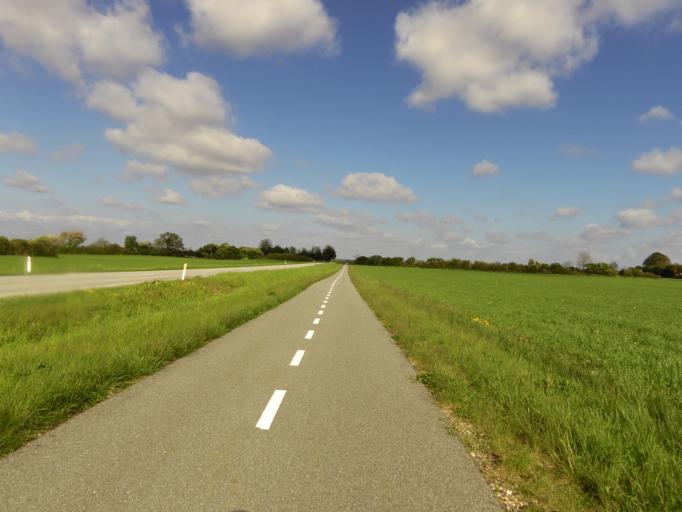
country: DK
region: South Denmark
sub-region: Vejen Kommune
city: Rodding
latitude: 55.3602
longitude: 9.0123
